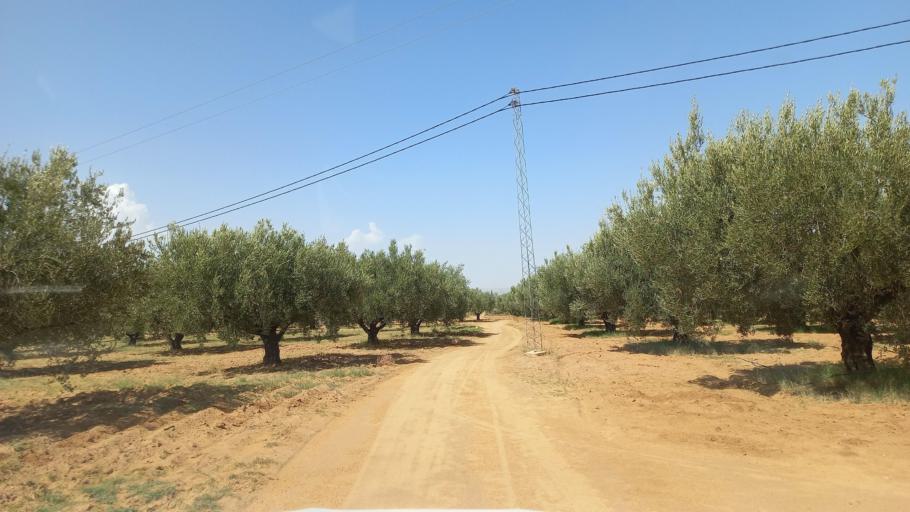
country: TN
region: Al Qasrayn
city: Kasserine
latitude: 35.2219
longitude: 9.0429
